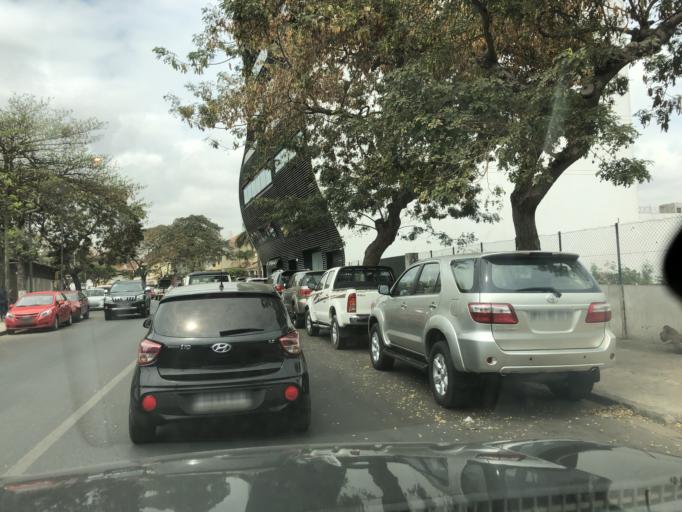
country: AO
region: Luanda
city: Luanda
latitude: -8.8261
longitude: 13.2352
